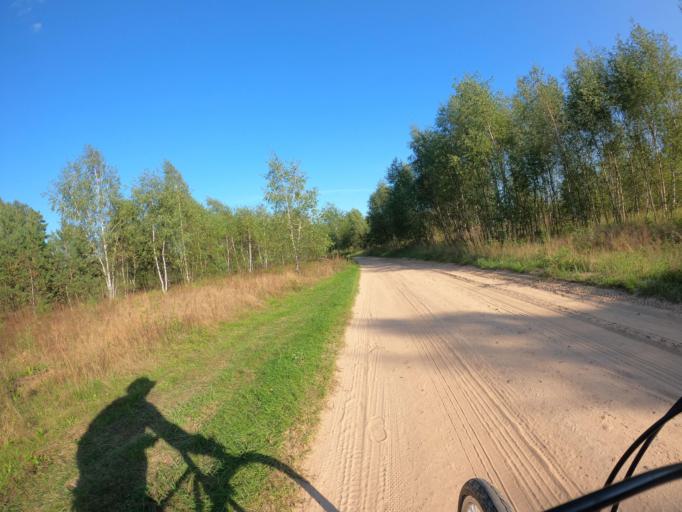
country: RU
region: Moskovskaya
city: Stupino
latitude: 54.8676
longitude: 38.1098
